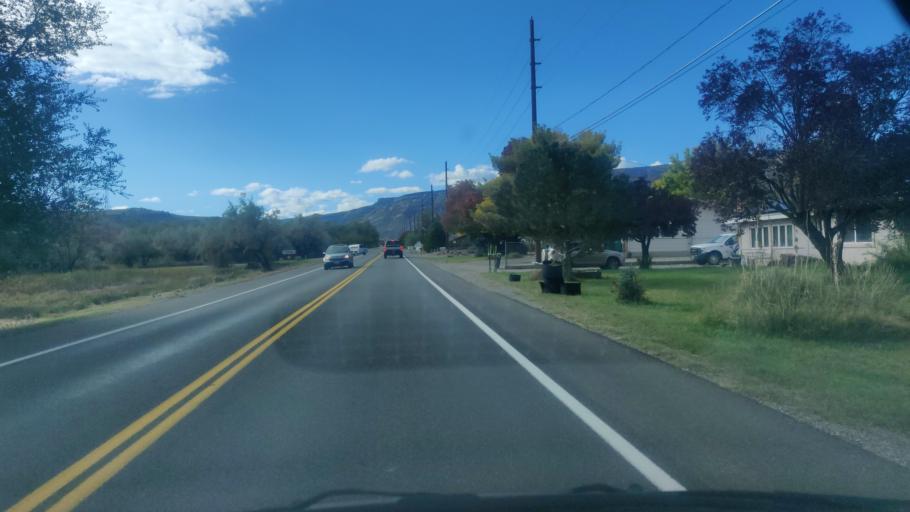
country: US
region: Colorado
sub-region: Mesa County
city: Redlands
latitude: 39.0704
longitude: -108.6450
